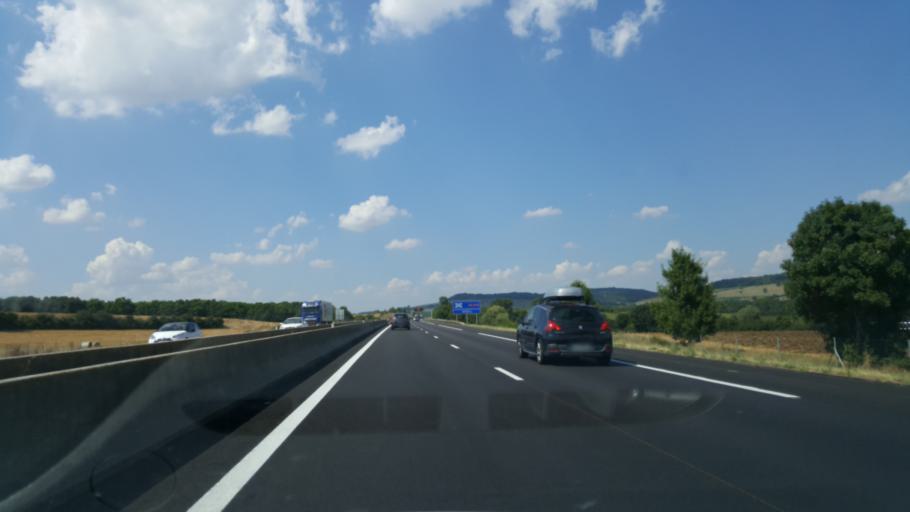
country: FR
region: Bourgogne
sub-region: Departement de la Cote-d'Or
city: Pouilly-en-Auxois
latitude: 47.2296
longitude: 4.5861
